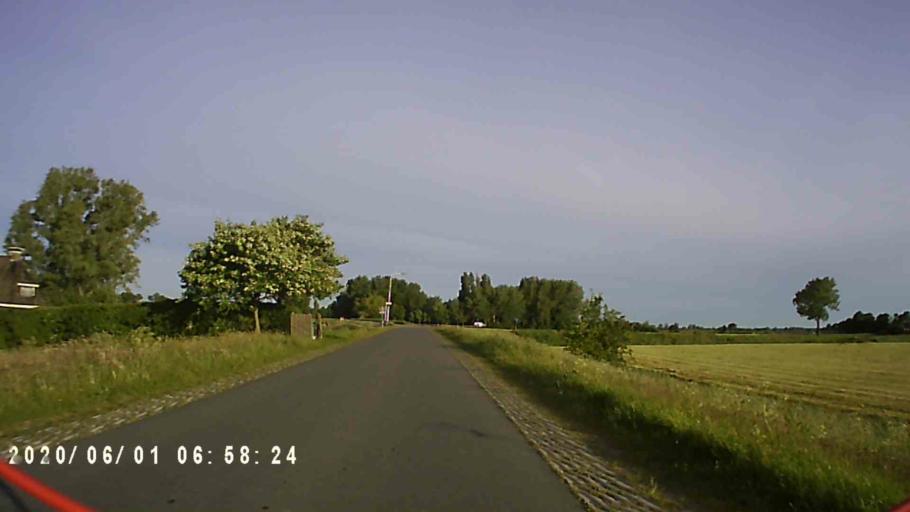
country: NL
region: Friesland
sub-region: Gemeente Dongeradeel
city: Anjum
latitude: 53.3195
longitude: 6.1009
